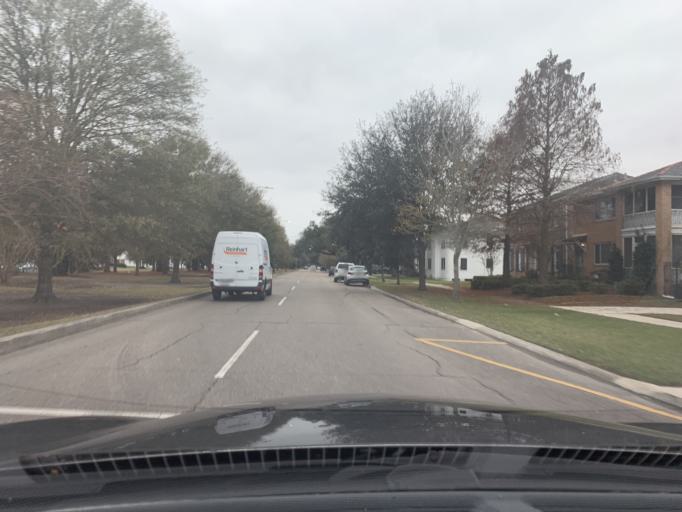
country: US
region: Louisiana
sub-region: Jefferson Parish
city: Metairie
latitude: 30.0177
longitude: -90.1067
